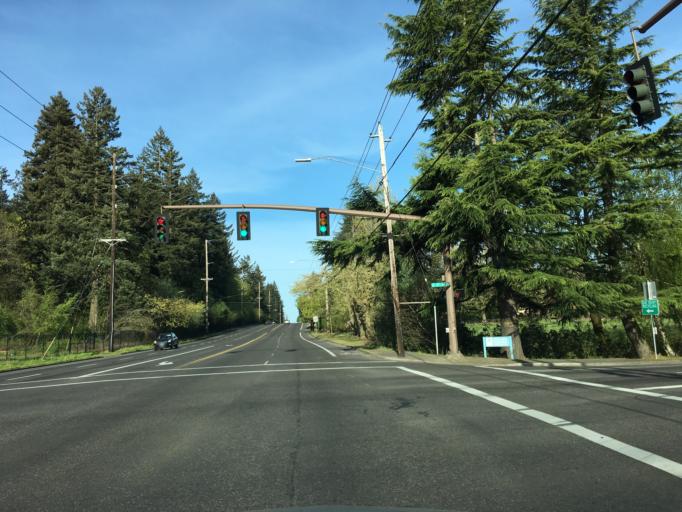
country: US
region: Oregon
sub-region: Multnomah County
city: Fairview
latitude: 45.5337
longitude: -122.5089
